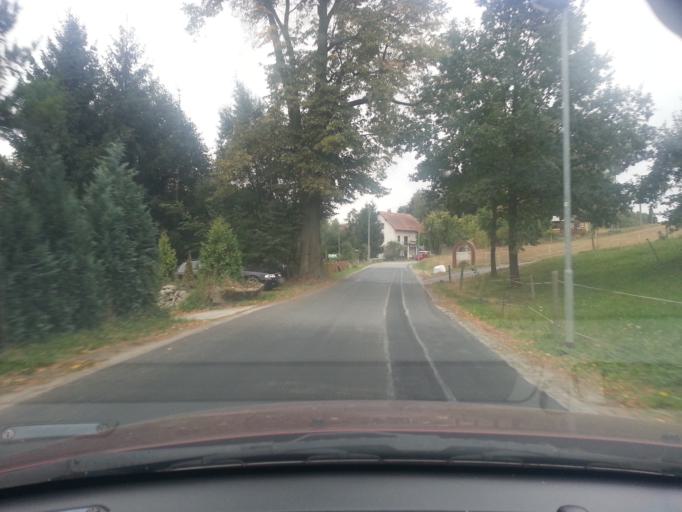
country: DE
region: Saxony
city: Schonau-Berzdorf
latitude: 51.0949
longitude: 14.8673
